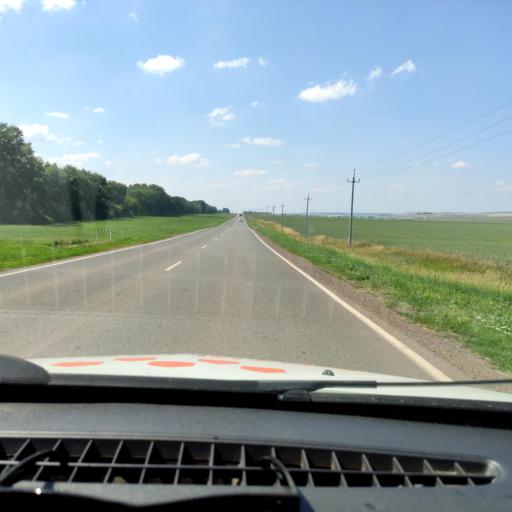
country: RU
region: Bashkortostan
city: Chekmagush
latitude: 55.1133
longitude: 54.8854
